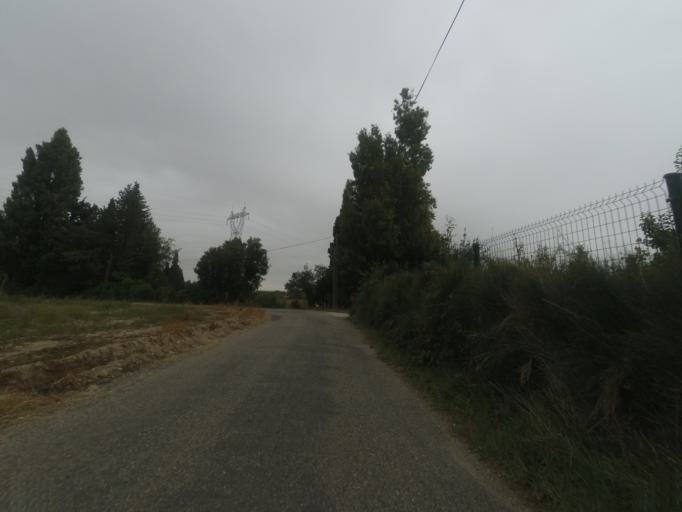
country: FR
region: Languedoc-Roussillon
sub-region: Departement des Pyrenees-Orientales
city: Saint-Esteve
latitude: 42.7017
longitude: 2.8420
